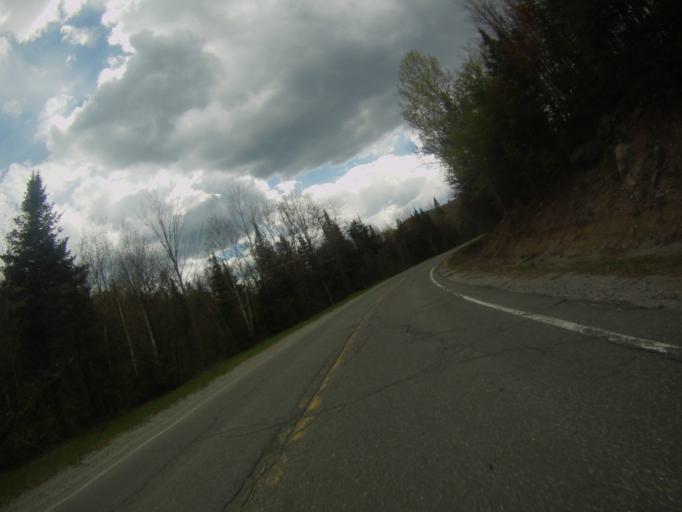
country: US
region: New York
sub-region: Essex County
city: Mineville
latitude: 44.0912
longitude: -73.5795
